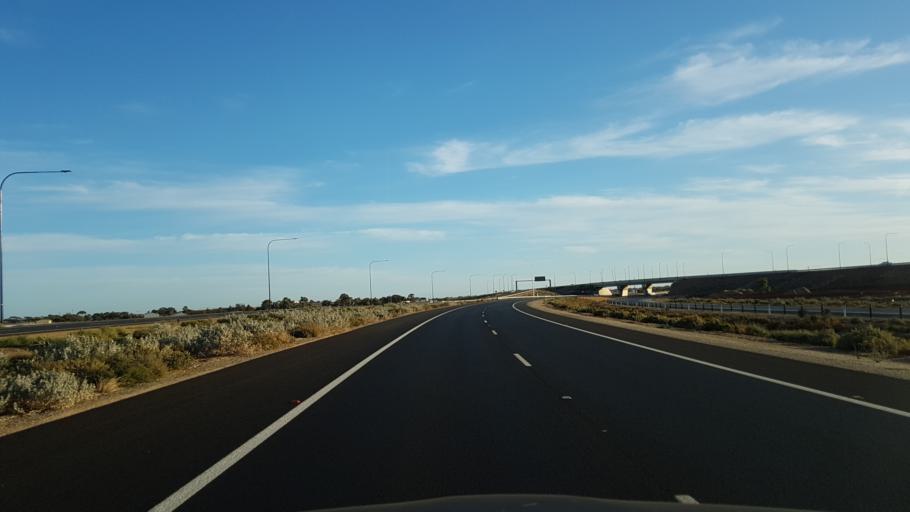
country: AU
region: South Australia
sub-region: Playford
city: Virginia
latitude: -34.7092
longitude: 138.5709
